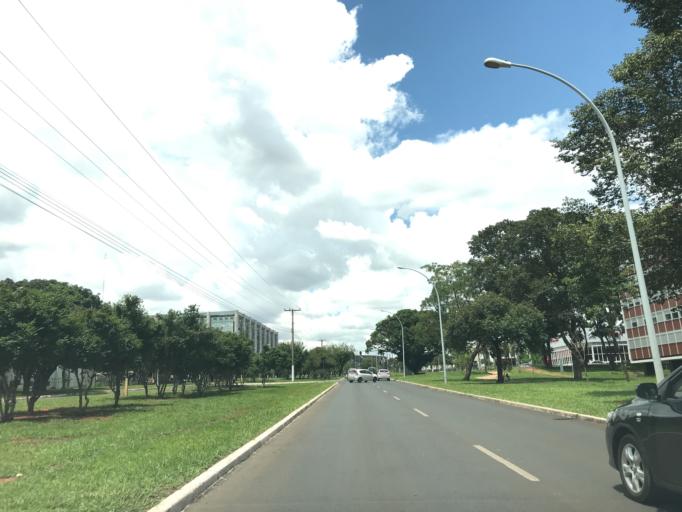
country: BR
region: Federal District
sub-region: Brasilia
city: Brasilia
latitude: -15.7834
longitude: -47.8856
